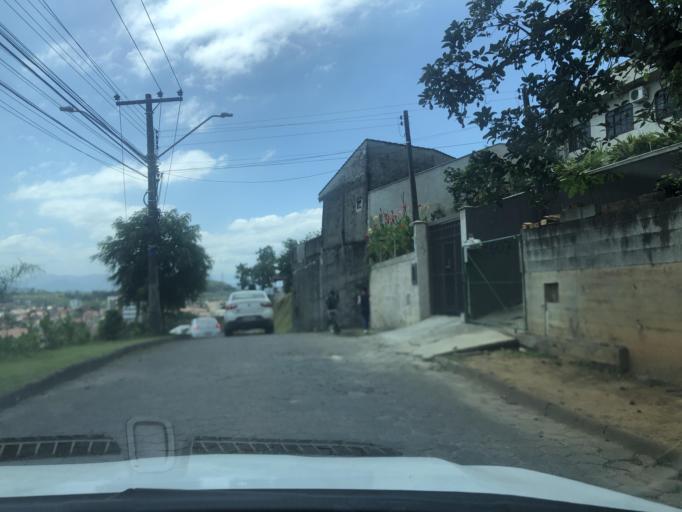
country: BR
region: Santa Catarina
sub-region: Joinville
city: Joinville
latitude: -26.3348
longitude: -48.8109
